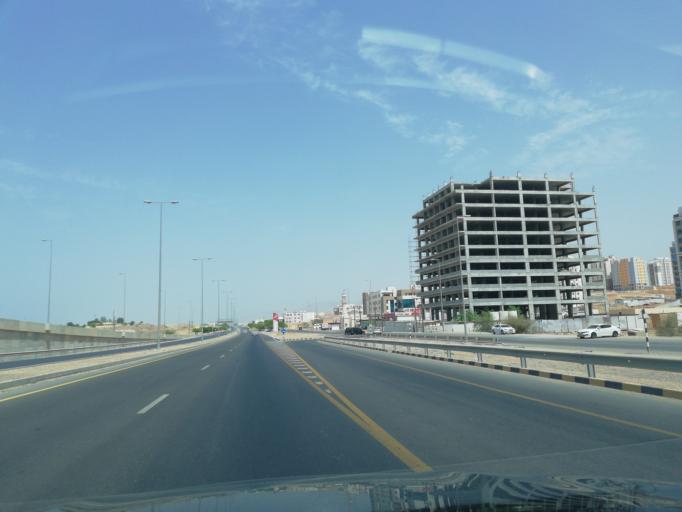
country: OM
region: Muhafazat Masqat
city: Bawshar
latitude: 23.5830
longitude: 58.3367
